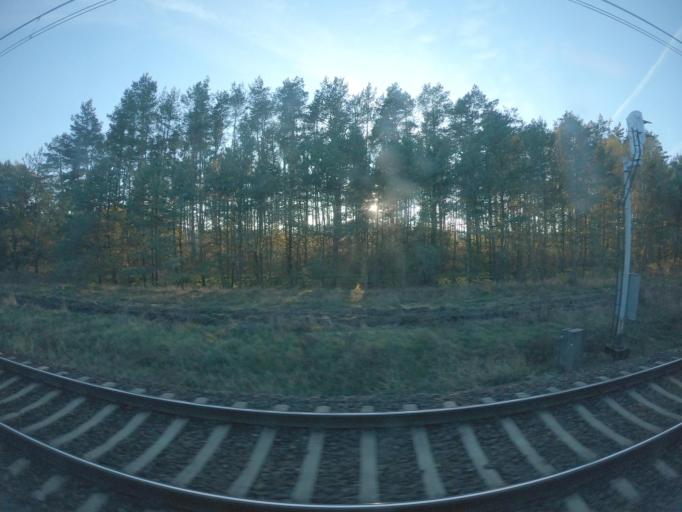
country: PL
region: Lubusz
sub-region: Powiat slubicki
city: Rzepin
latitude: 52.2632
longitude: 14.9398
